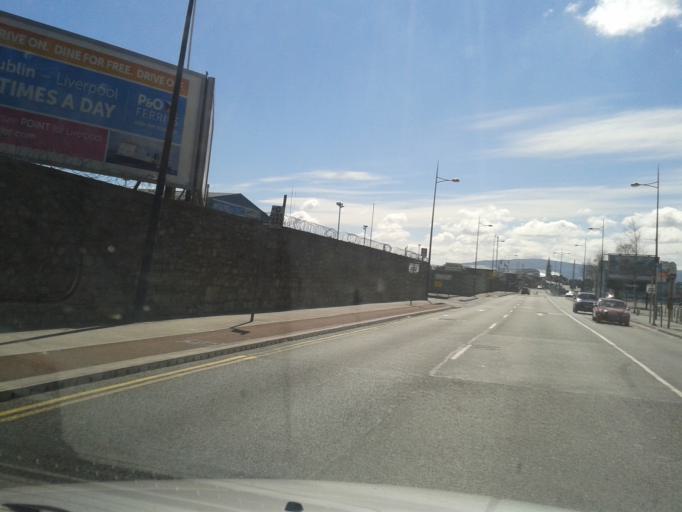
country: IE
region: Leinster
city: Ringsend
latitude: 53.3489
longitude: -6.2269
